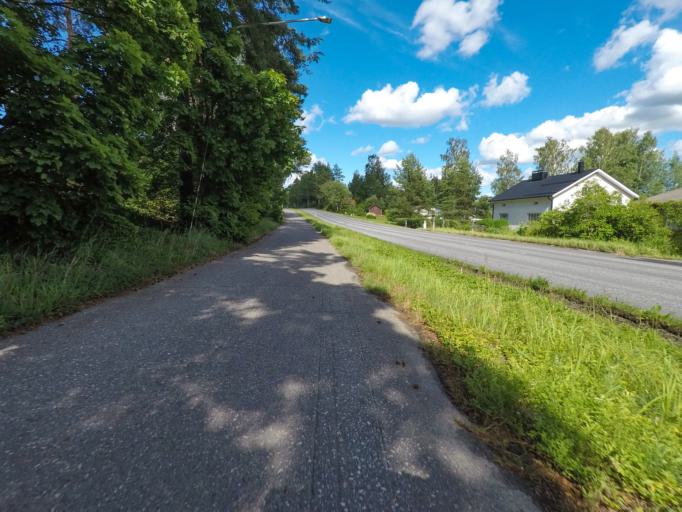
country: FI
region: South Karelia
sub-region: Lappeenranta
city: Lappeenranta
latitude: 61.0806
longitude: 28.3285
